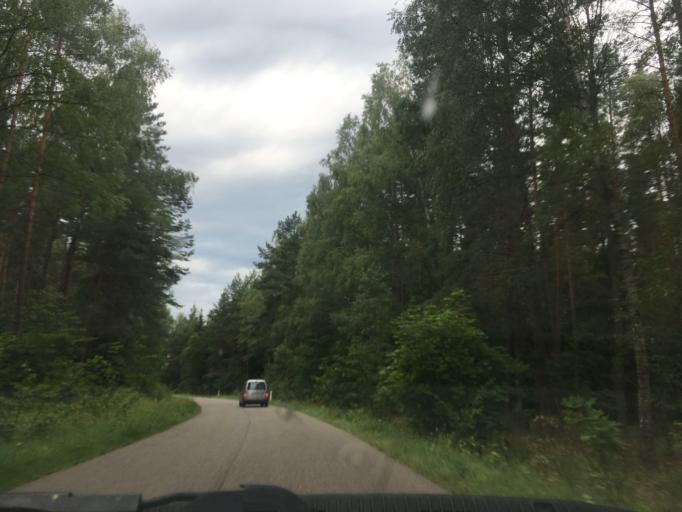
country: PL
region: Warmian-Masurian Voivodeship
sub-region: Powiat wegorzewski
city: Pozezdrze
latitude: 54.1277
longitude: 21.8269
